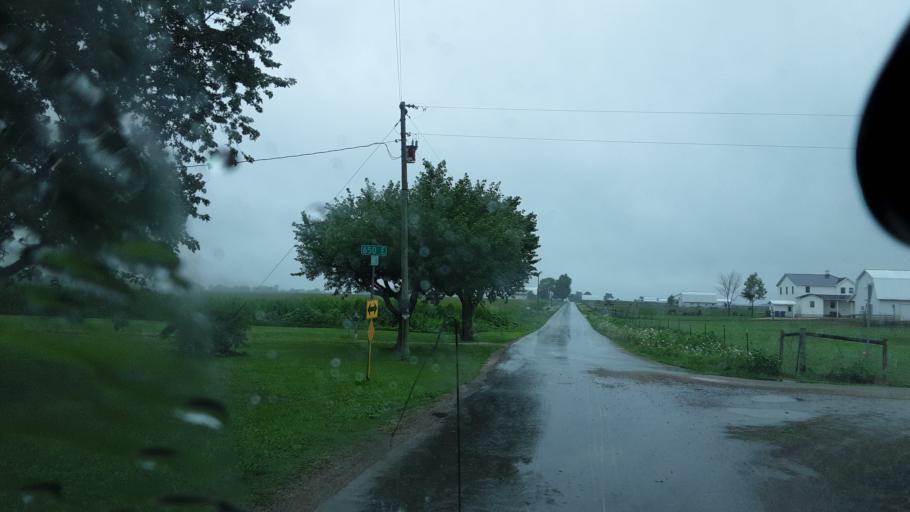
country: US
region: Indiana
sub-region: Adams County
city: Berne
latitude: 40.6892
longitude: -84.8116
